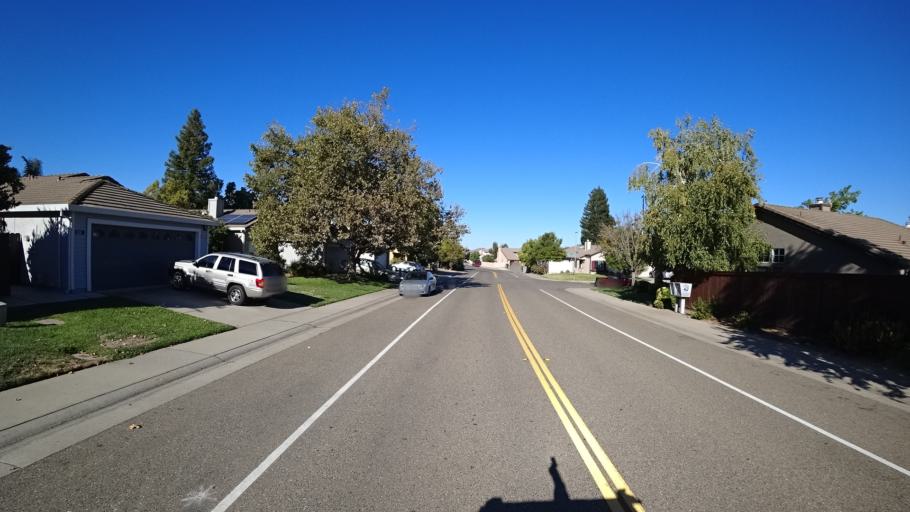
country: US
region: California
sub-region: Sacramento County
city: Vineyard
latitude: 38.4488
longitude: -121.3609
